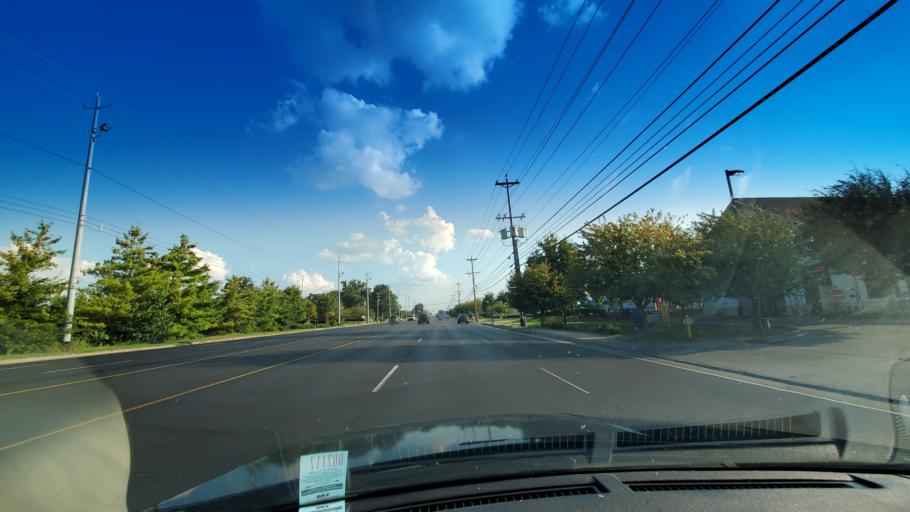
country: US
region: Tennessee
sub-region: Rutherford County
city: Murfreesboro
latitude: 35.7924
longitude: -86.3997
